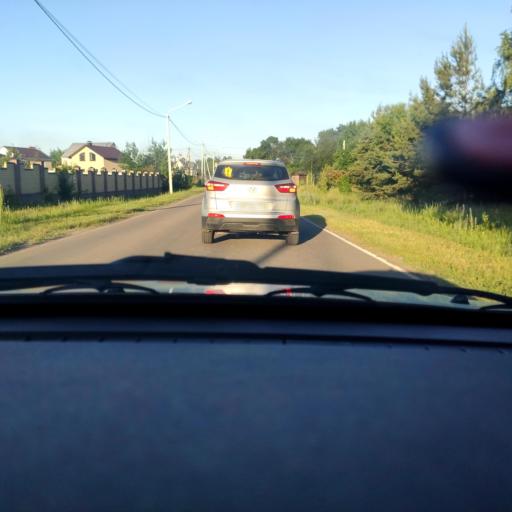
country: RU
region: Voronezj
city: Ramon'
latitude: 51.8905
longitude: 39.2634
